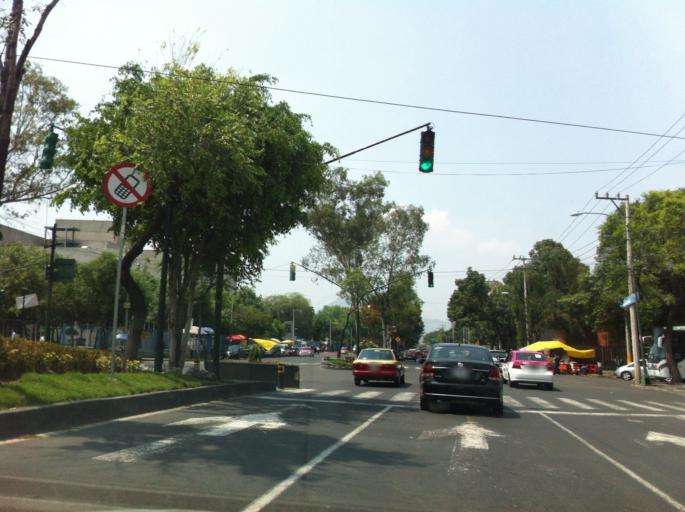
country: MX
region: Mexico
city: Colonia Lindavista
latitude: 19.4796
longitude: -99.1357
